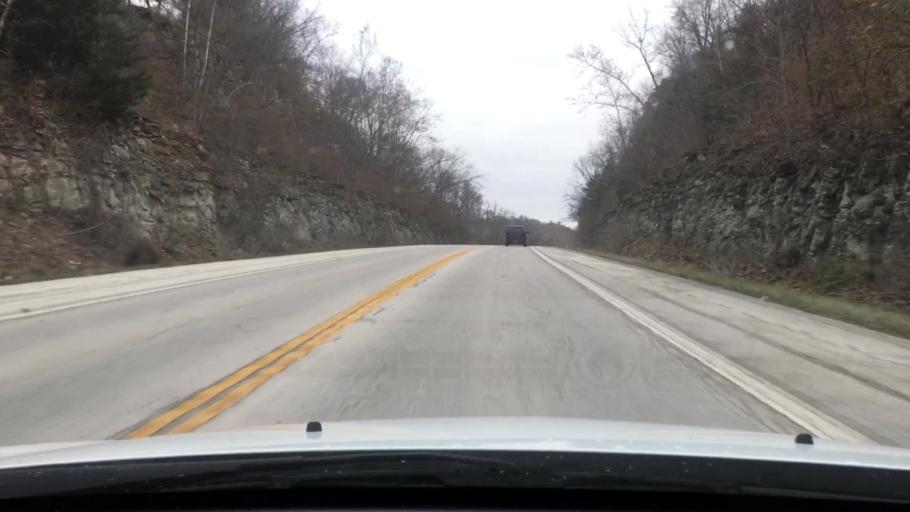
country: US
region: Missouri
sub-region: Pike County
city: Louisiana
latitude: 39.4414
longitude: -91.0784
